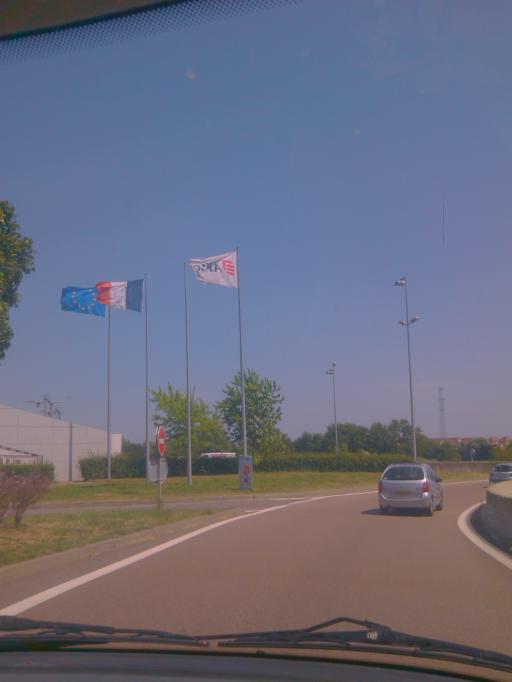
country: FR
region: Bourgogne
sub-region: Departement de Saone-et-Loire
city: Saint-Remy
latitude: 46.7555
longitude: 4.8322
